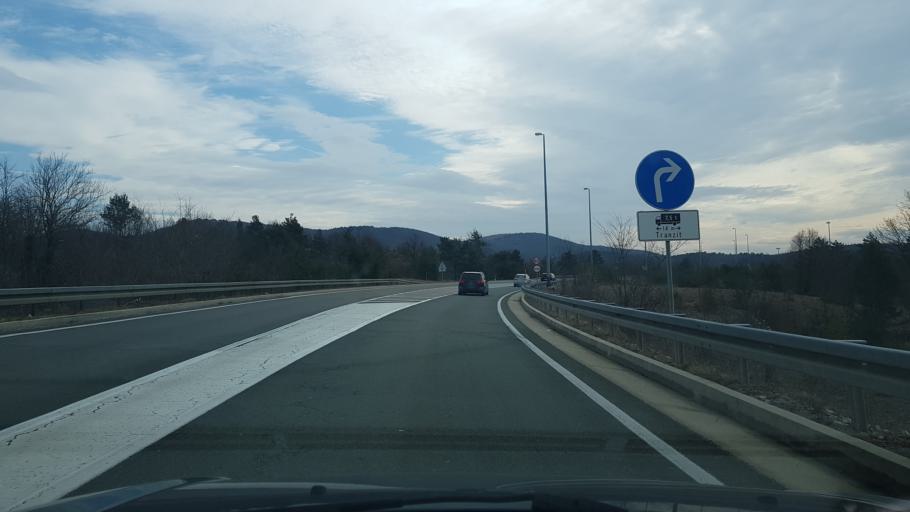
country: SI
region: Ilirska Bistrica
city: Ilirska Bistrica
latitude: 45.4760
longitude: 14.2709
